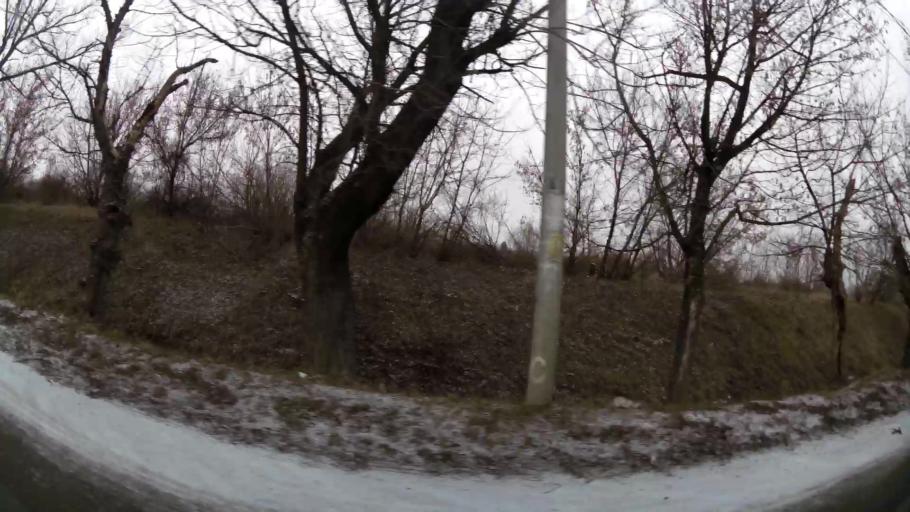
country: RO
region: Dambovita
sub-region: Municipiul Targoviste
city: Targoviste
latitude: 44.9293
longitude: 25.4791
